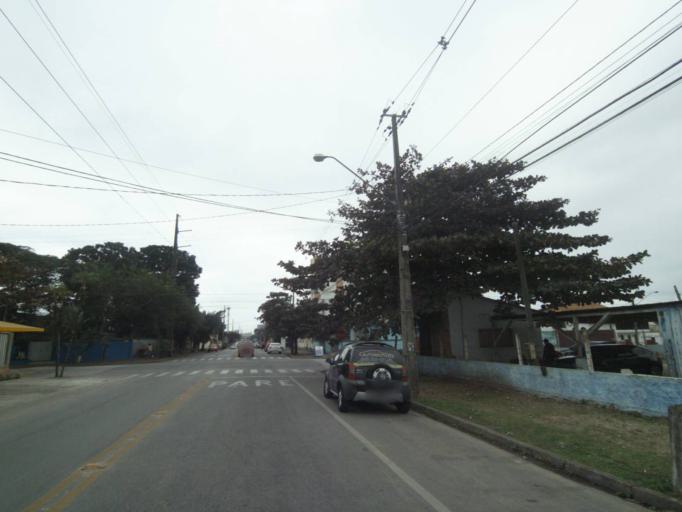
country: BR
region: Parana
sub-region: Paranagua
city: Paranagua
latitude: -25.5156
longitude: -48.5169
